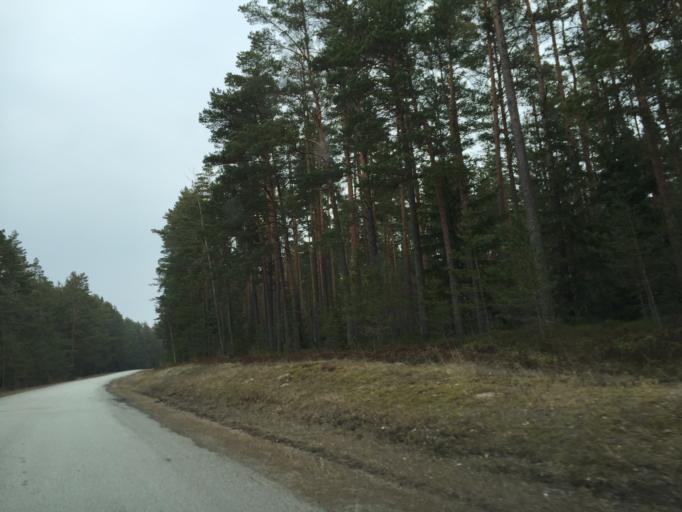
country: LV
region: Salacgrivas
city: Ainazi
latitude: 57.9812
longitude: 24.4164
